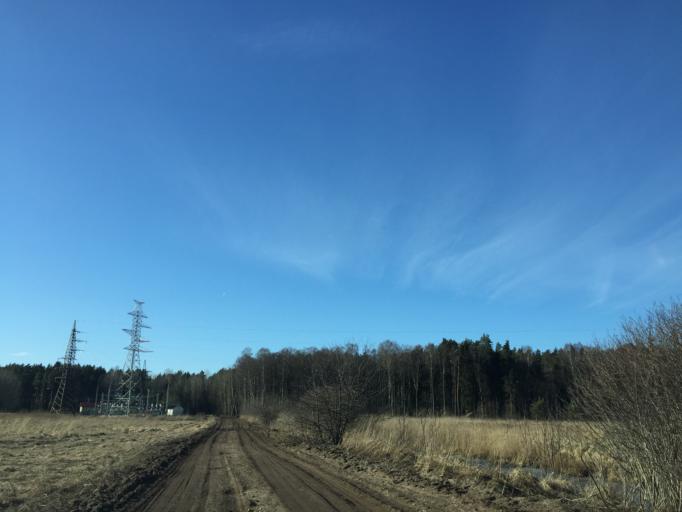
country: LV
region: Babite
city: Pinki
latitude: 56.9652
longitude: 23.8878
